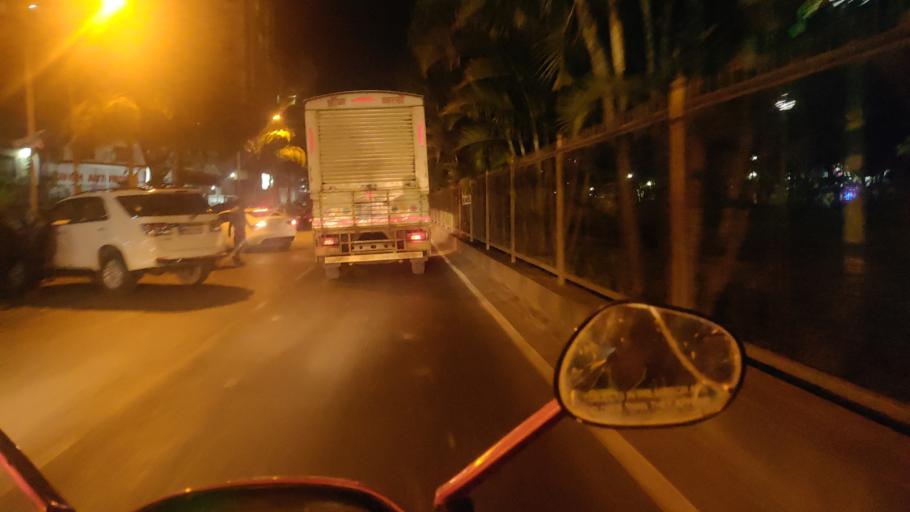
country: IN
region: Maharashtra
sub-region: Thane
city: Bhayandar
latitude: 19.2945
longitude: 72.8475
